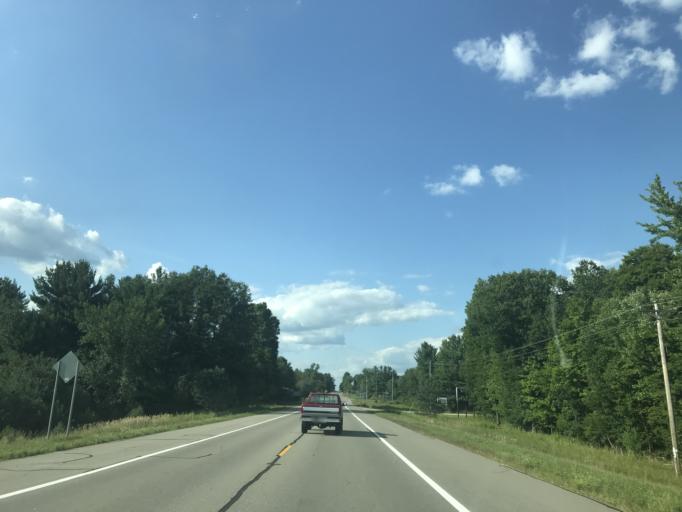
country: US
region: Michigan
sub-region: Newaygo County
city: White Cloud
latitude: 43.5654
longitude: -85.7715
